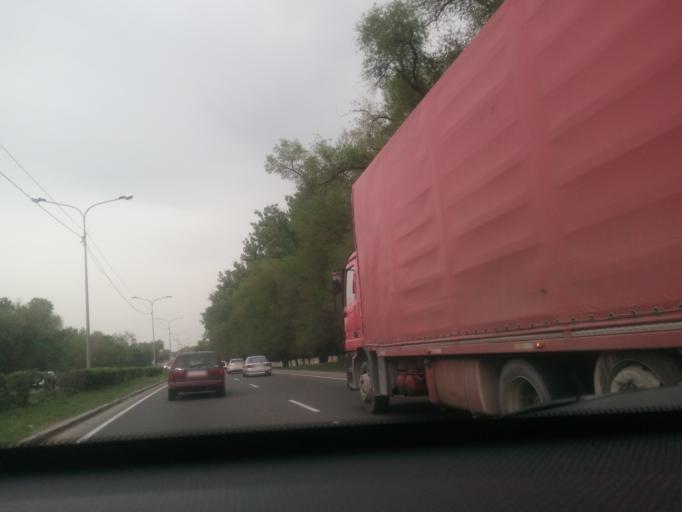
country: KZ
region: Almaty Oblysy
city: Burunday
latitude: 43.2205
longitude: 76.7140
